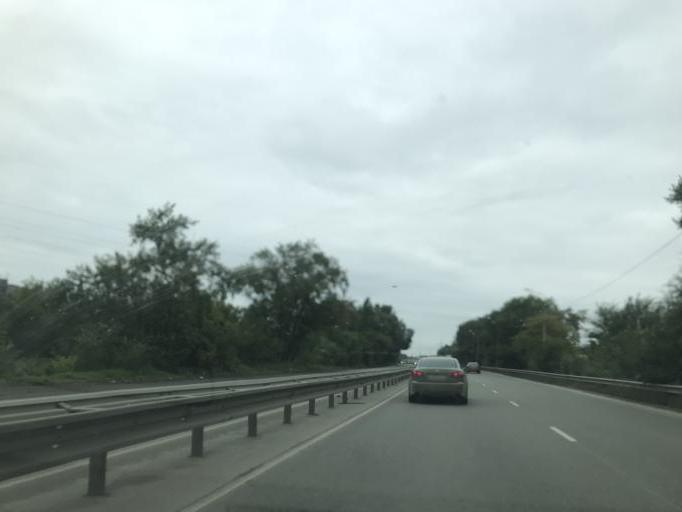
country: RU
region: Chelyabinsk
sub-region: Gorod Chelyabinsk
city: Chelyabinsk
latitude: 55.1703
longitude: 61.4279
